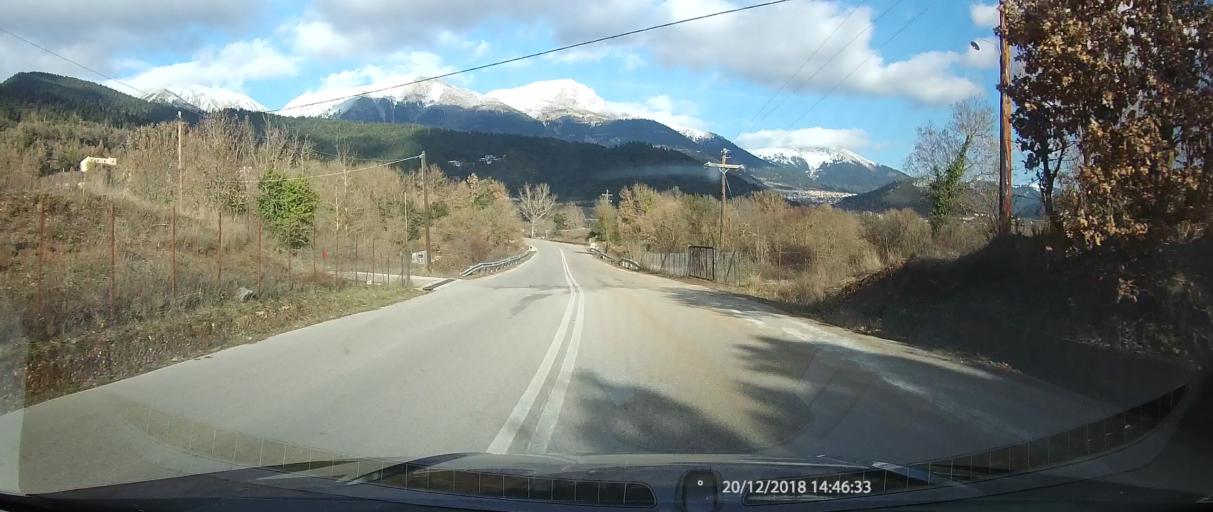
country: GR
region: Central Greece
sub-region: Nomos Evrytanias
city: Karpenisi
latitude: 38.8969
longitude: 21.7685
